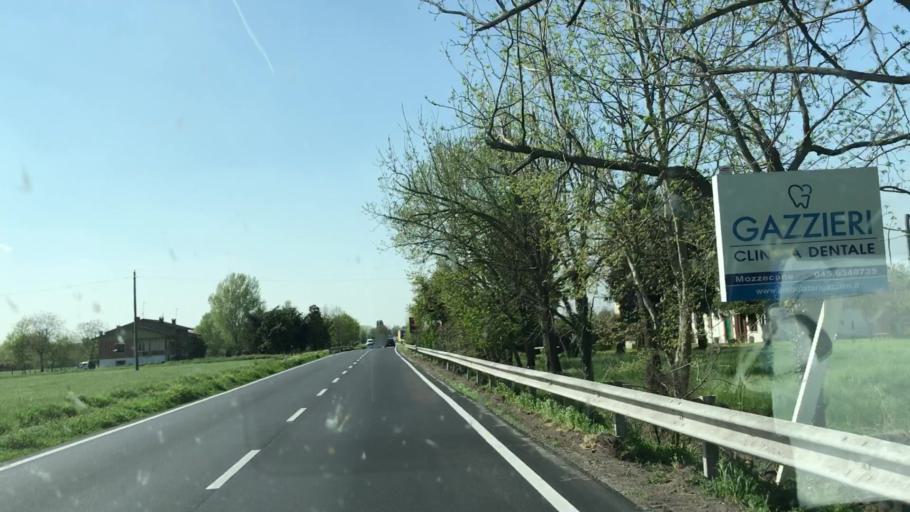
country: IT
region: Lombardy
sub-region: Provincia di Mantova
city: Marmirolo
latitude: 45.2228
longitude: 10.7378
